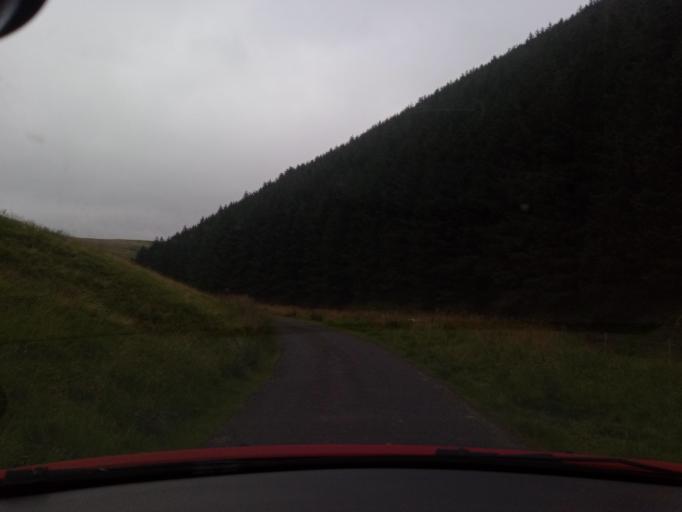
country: GB
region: England
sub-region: Northumberland
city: Rochester
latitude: 55.3944
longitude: -2.2611
